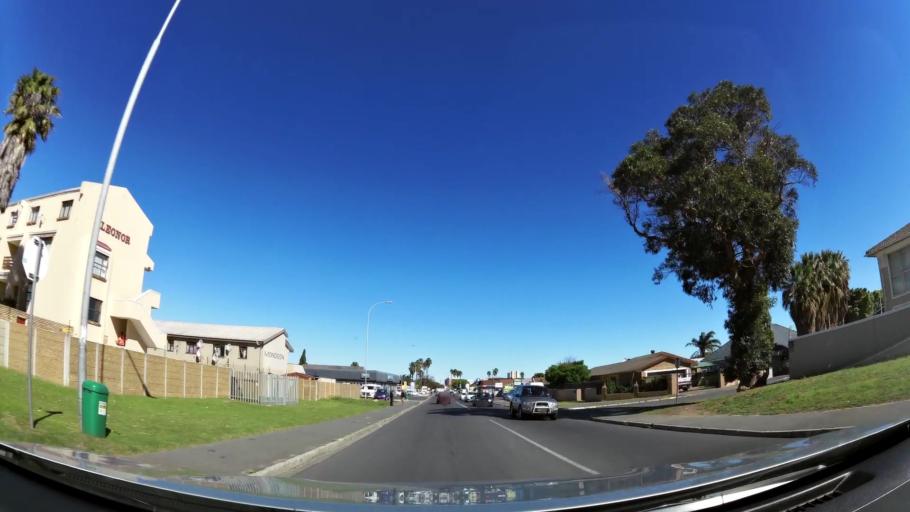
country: ZA
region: Western Cape
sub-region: Cape Winelands District Municipality
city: Stellenbosch
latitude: -34.1090
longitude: 18.8371
